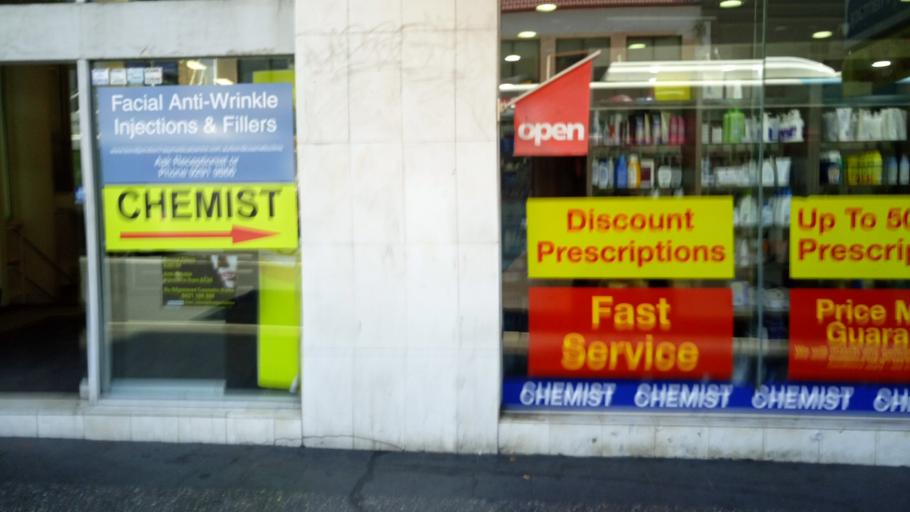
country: AU
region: New South Wales
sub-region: Waverley
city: Bondi Junction
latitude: -33.8917
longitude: 151.2472
